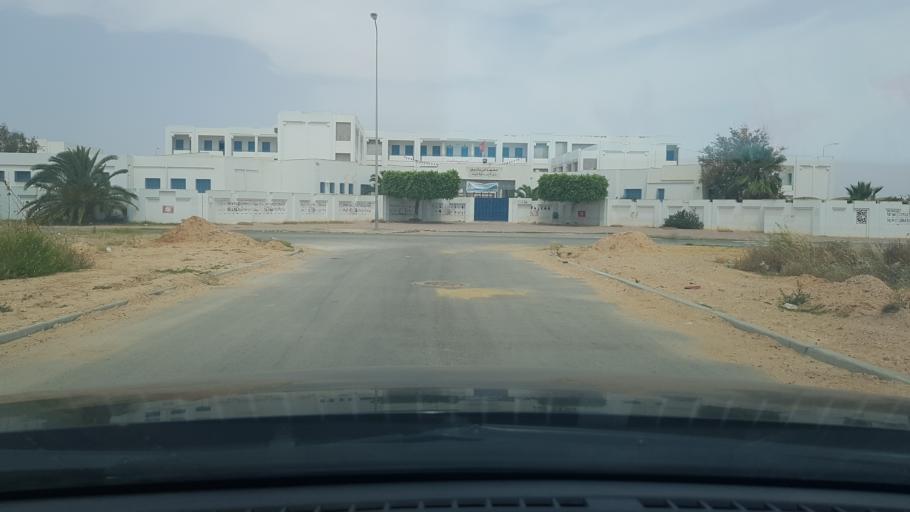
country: TN
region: Safaqis
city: Al Qarmadah
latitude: 34.8250
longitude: 10.7442
